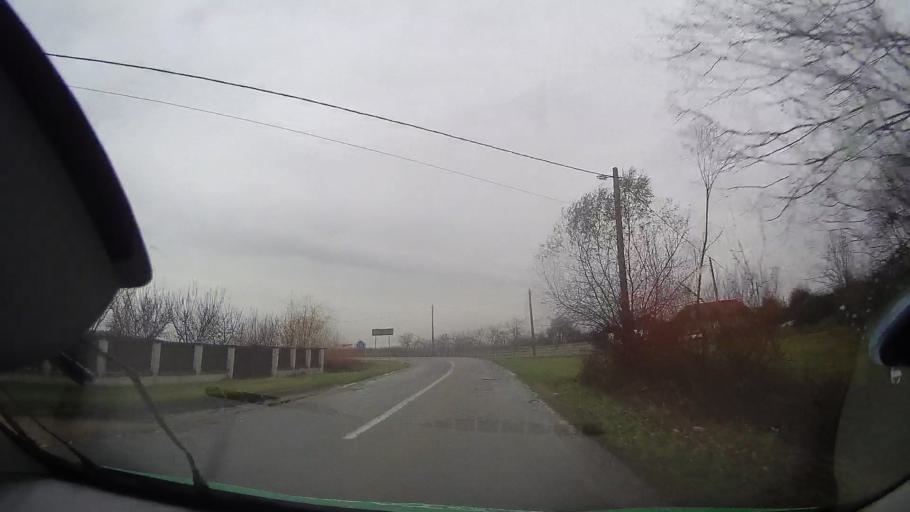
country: RO
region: Bihor
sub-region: Comuna Cociuba Mare
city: Cociuba Mare
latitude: 46.7398
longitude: 21.9870
